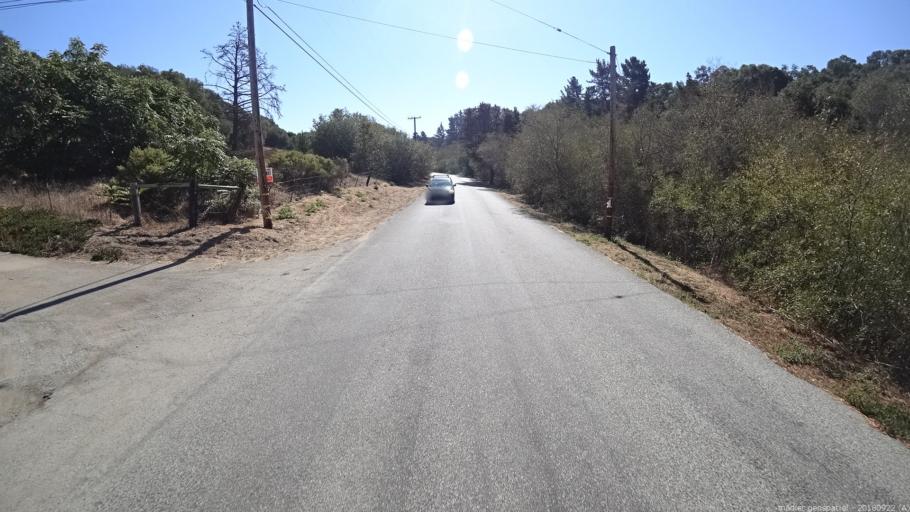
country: US
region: California
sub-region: Monterey County
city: Prunedale
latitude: 36.8127
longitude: -121.6399
